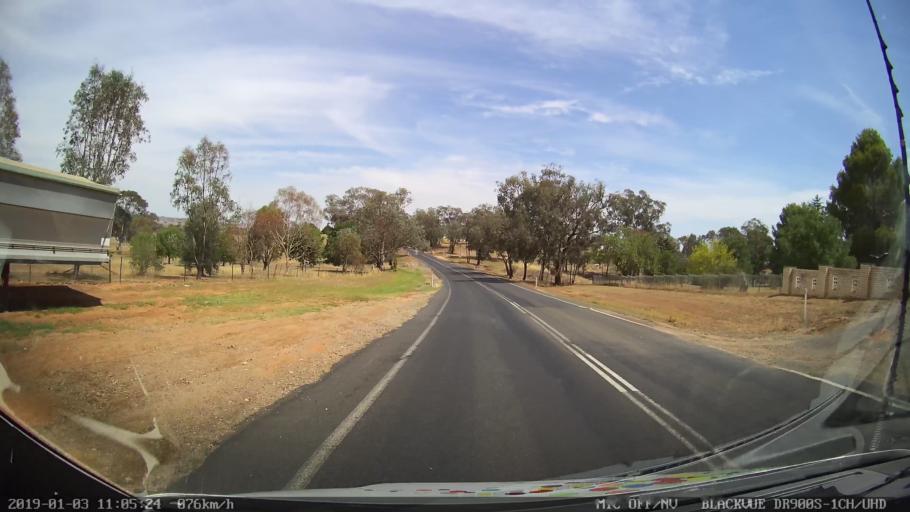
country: AU
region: New South Wales
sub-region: Young
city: Young
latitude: -34.2721
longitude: 148.2853
